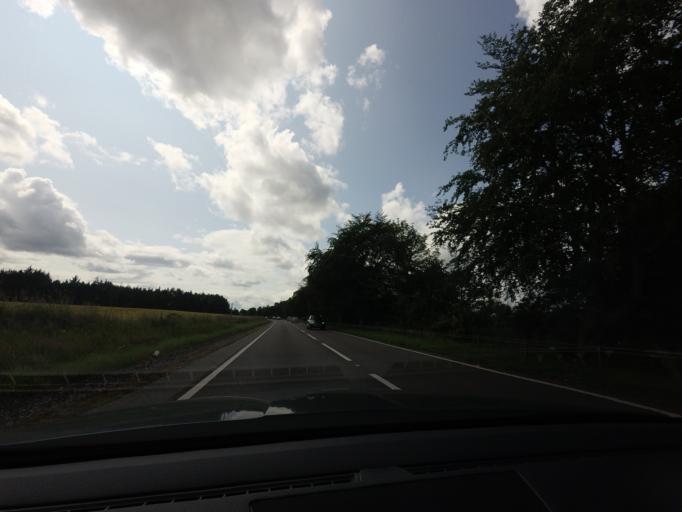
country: GB
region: Scotland
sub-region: Moray
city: Forres
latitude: 57.5999
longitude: -3.6687
